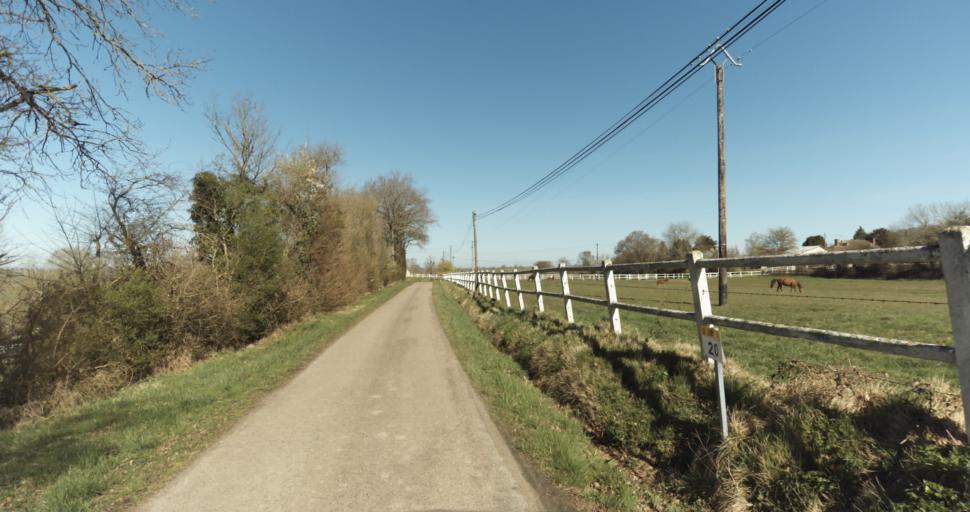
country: FR
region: Lower Normandy
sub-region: Departement de l'Orne
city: Trun
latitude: 48.9303
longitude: 0.0459
